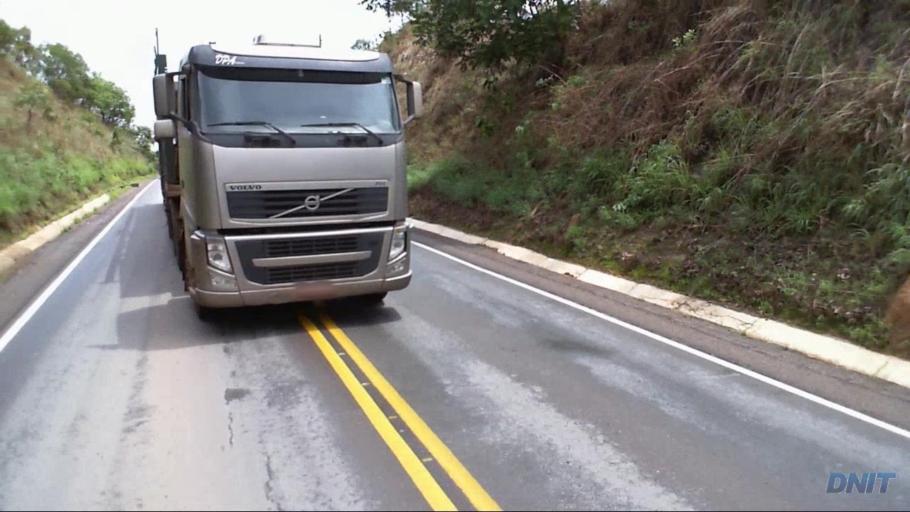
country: BR
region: Goias
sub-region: Padre Bernardo
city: Padre Bernardo
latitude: -15.4765
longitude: -48.2323
